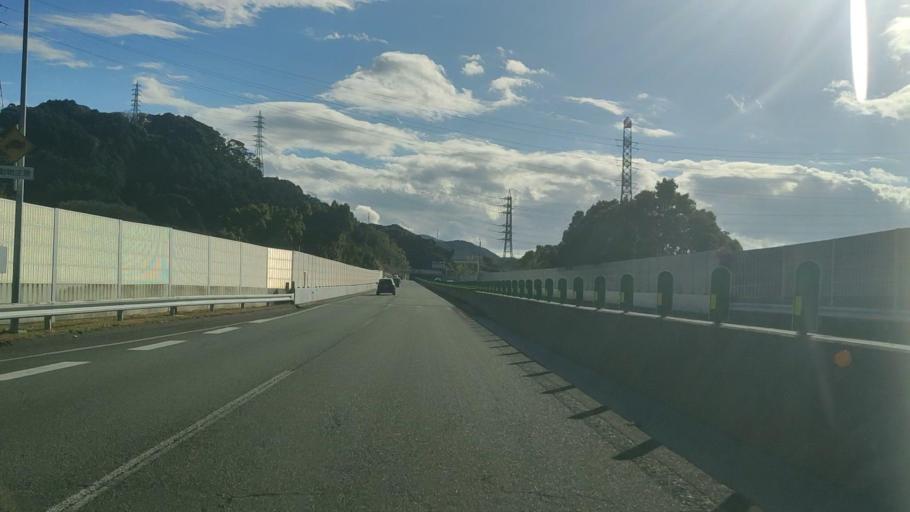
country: JP
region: Fukuoka
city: Kitakyushu
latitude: 33.8378
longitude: 130.7654
